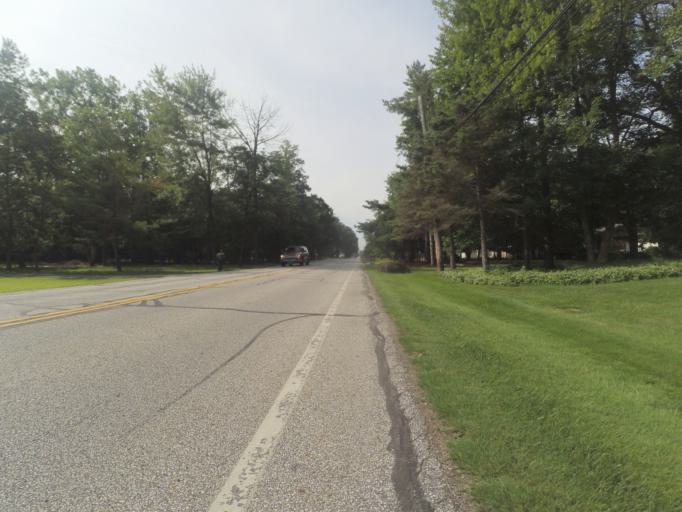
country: US
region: Ohio
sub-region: Cuyahoga County
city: Orange
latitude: 41.4531
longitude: -81.4802
